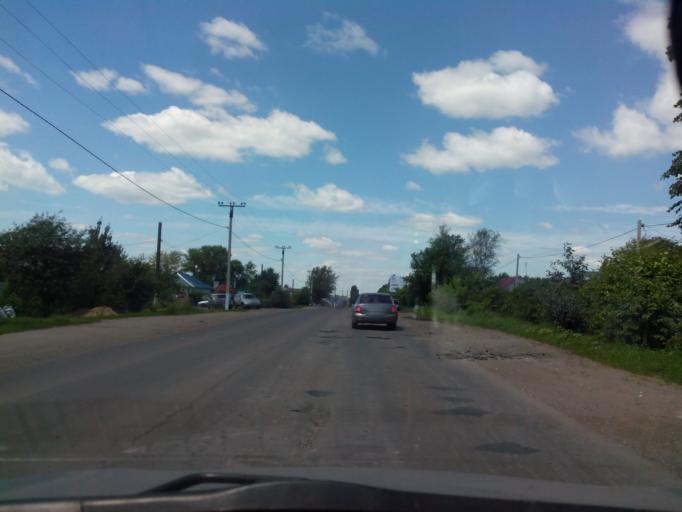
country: RU
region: Tambov
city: Zherdevka
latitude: 51.8264
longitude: 41.4962
